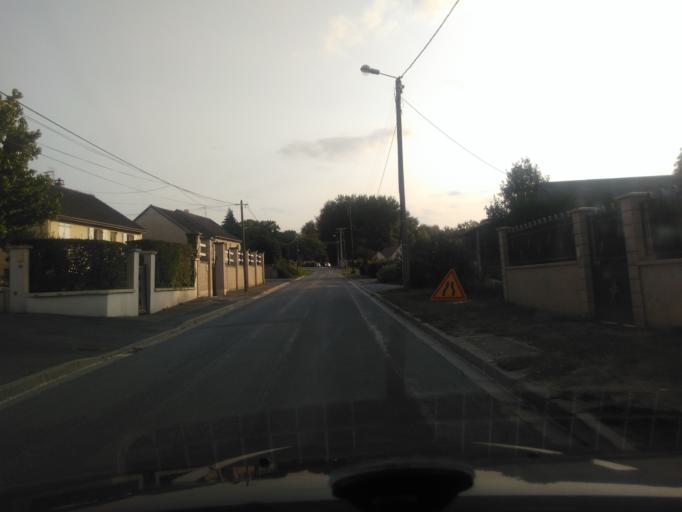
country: FR
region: Champagne-Ardenne
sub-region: Departement de la Marne
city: Fismes
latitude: 49.2667
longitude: 3.6989
